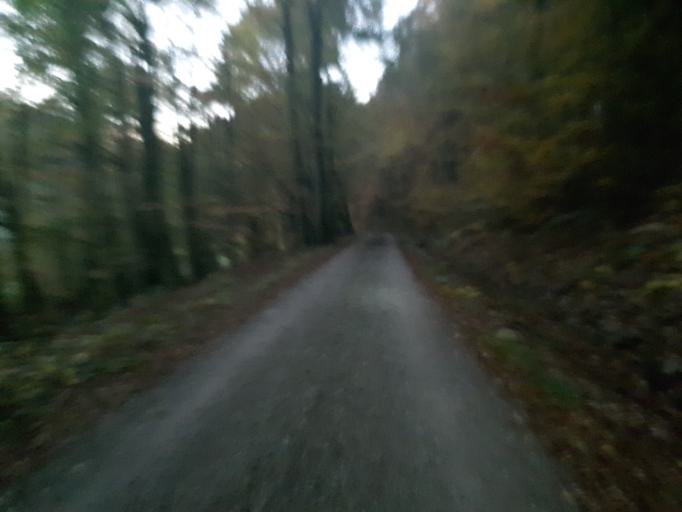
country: DE
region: Bavaria
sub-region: Regierungsbezirk Unterfranken
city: Leidersbach
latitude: 49.8951
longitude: 9.2550
